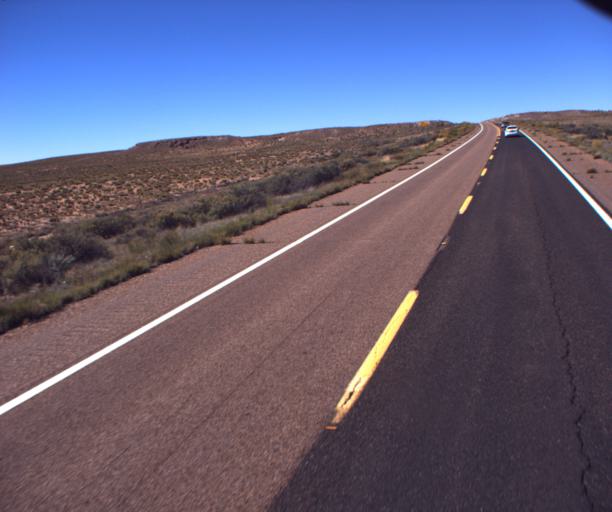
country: US
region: Arizona
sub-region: Navajo County
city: Holbrook
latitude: 34.7757
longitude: -109.8306
